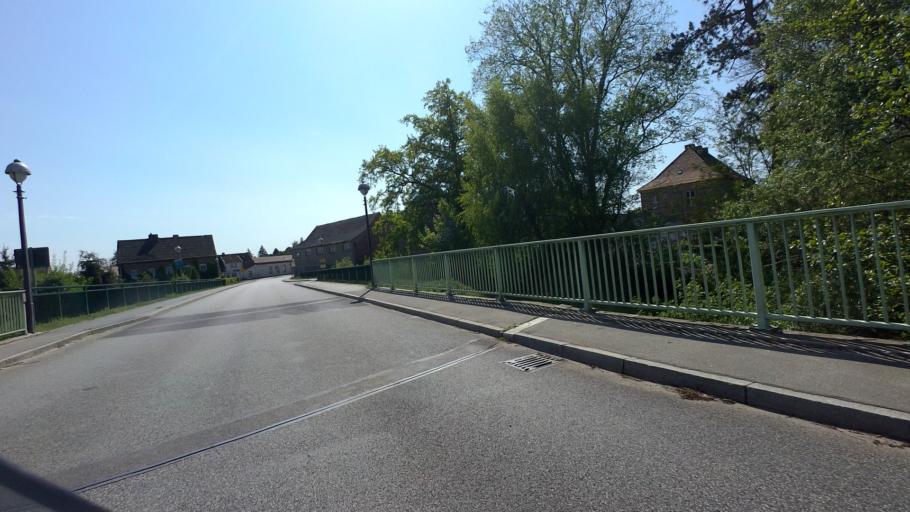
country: DE
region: Brandenburg
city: Tauche
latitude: 52.0848
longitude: 14.1704
